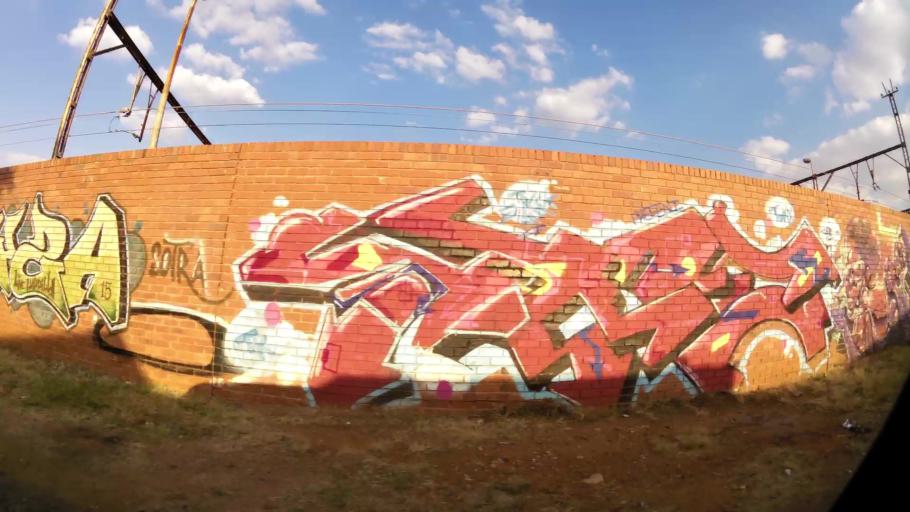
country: ZA
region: Gauteng
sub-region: City of Johannesburg Metropolitan Municipality
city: Soweto
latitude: -26.2346
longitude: 27.9051
